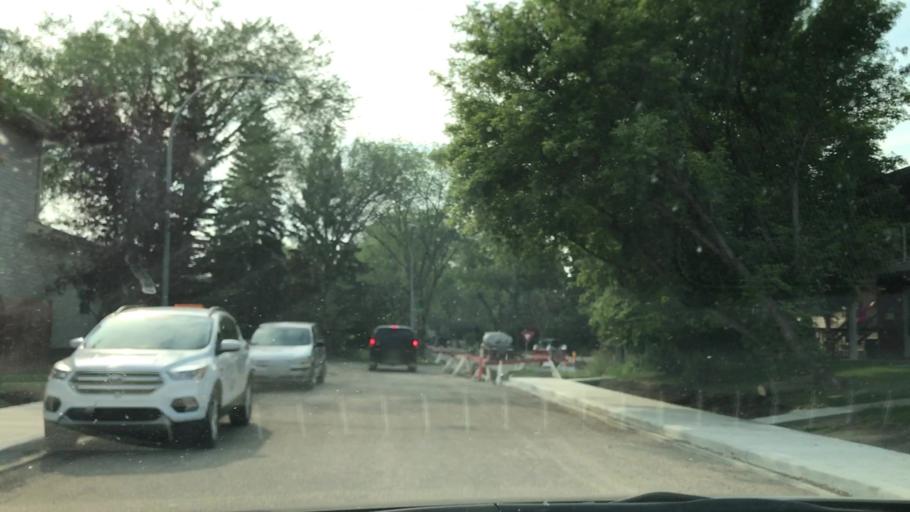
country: CA
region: Alberta
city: Edmonton
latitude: 53.5035
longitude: -113.4996
